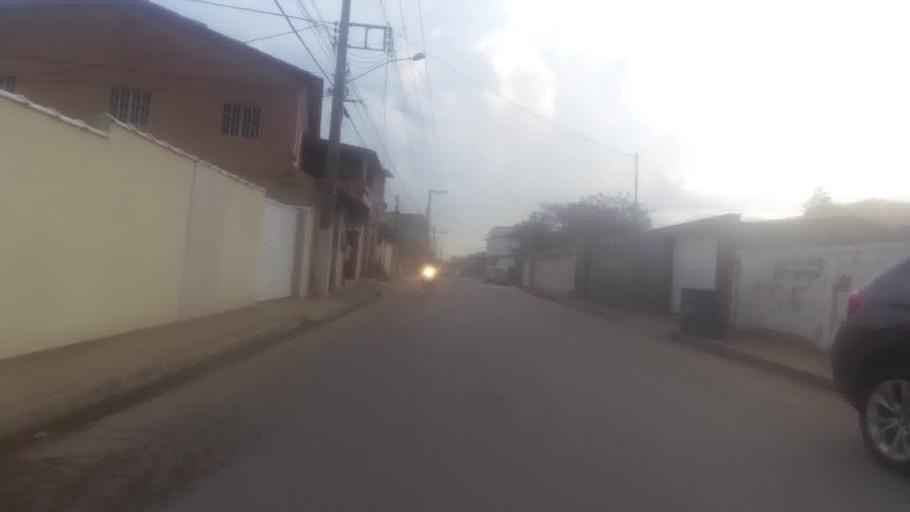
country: BR
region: Espirito Santo
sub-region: Piuma
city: Piuma
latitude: -20.8080
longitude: -40.6377
